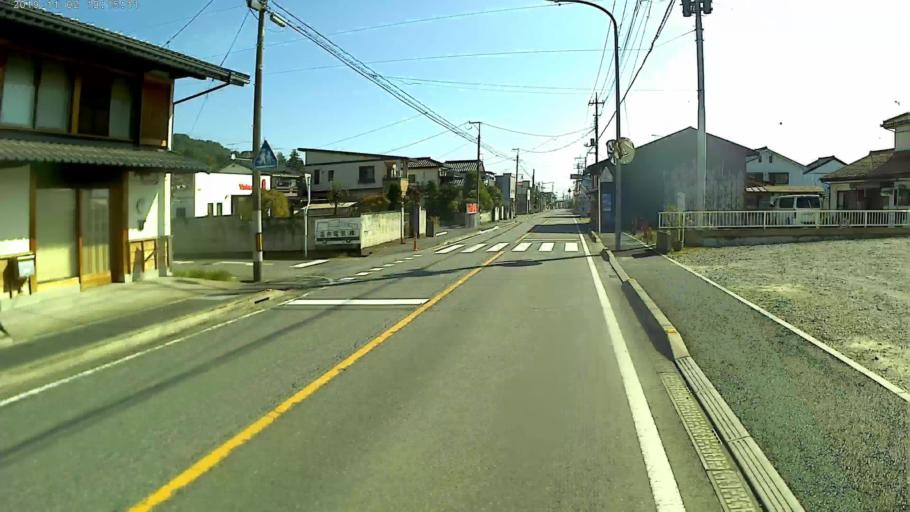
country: JP
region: Gunma
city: Annaka
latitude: 36.3158
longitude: 138.7946
